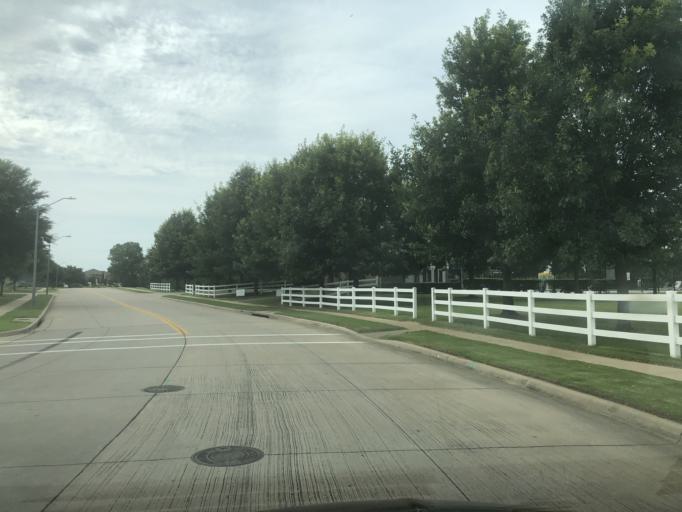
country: US
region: Texas
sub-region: Dallas County
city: Irving
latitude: 32.7992
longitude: -96.9920
